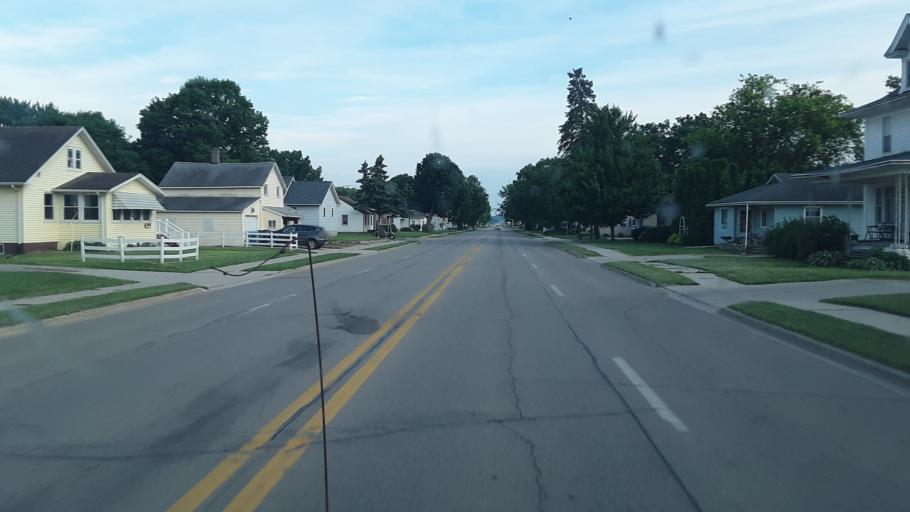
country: US
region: Iowa
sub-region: Benton County
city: Belle Plaine
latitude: 41.8939
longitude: -92.2782
